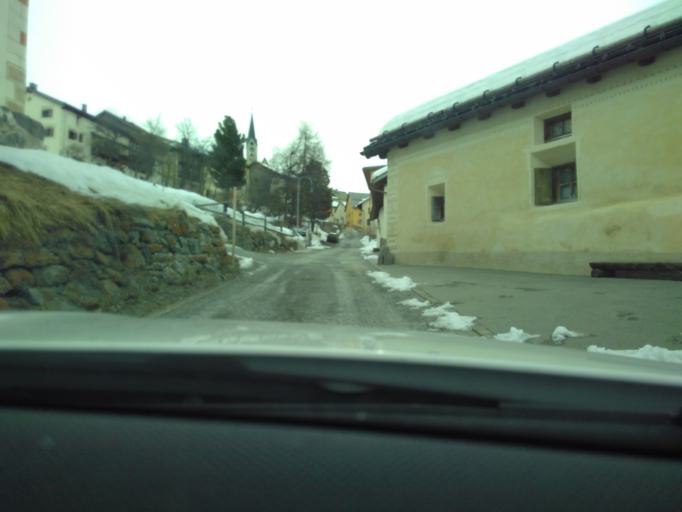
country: CH
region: Grisons
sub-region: Inn District
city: Zernez
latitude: 46.7755
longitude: 10.1499
